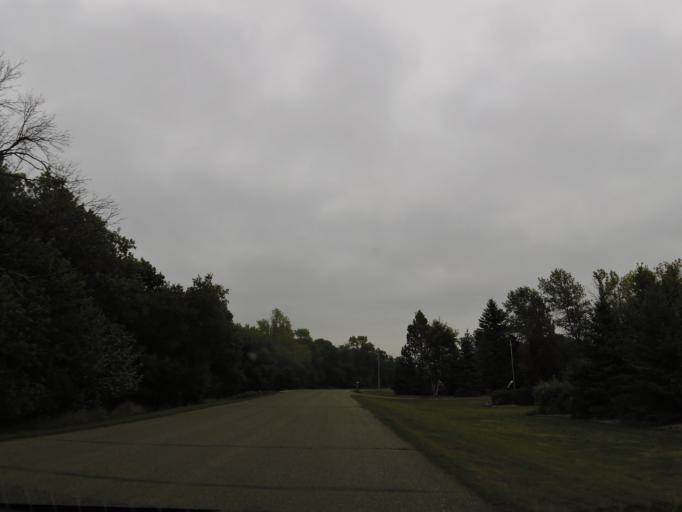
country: US
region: Minnesota
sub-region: Marshall County
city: Warren
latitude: 48.4468
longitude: -96.8810
